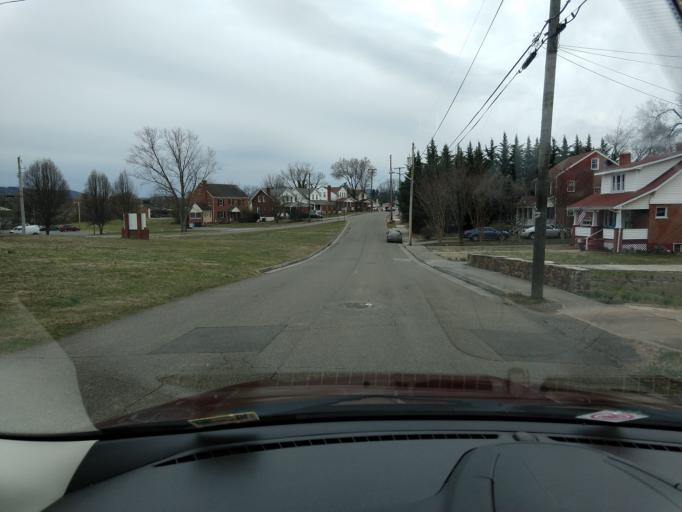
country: US
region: Virginia
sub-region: City of Roanoke
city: Roanoke
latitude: 37.3017
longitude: -79.9400
